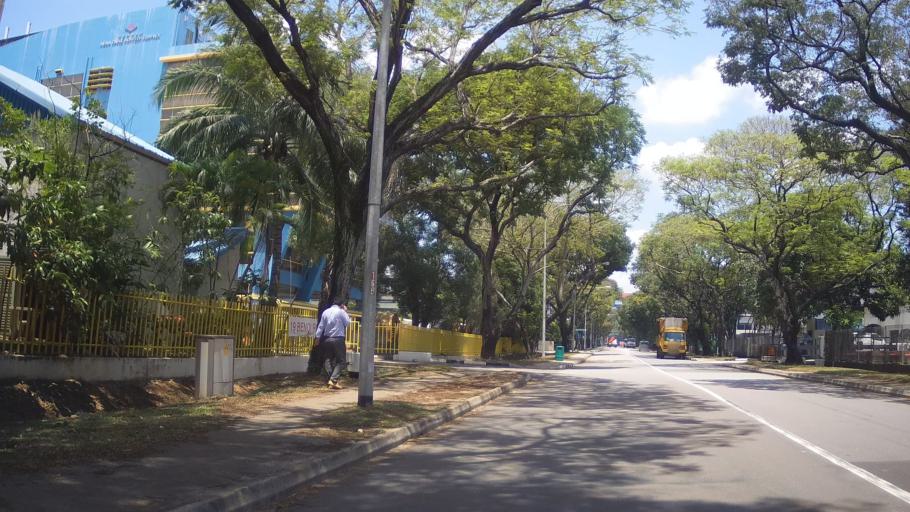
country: SG
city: Singapore
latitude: 1.3042
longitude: 103.6761
